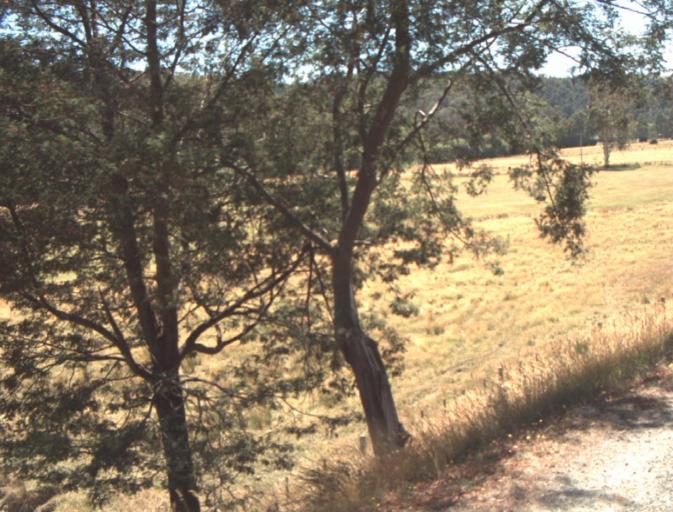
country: AU
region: Tasmania
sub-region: Dorset
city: Scottsdale
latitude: -41.3193
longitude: 147.3640
